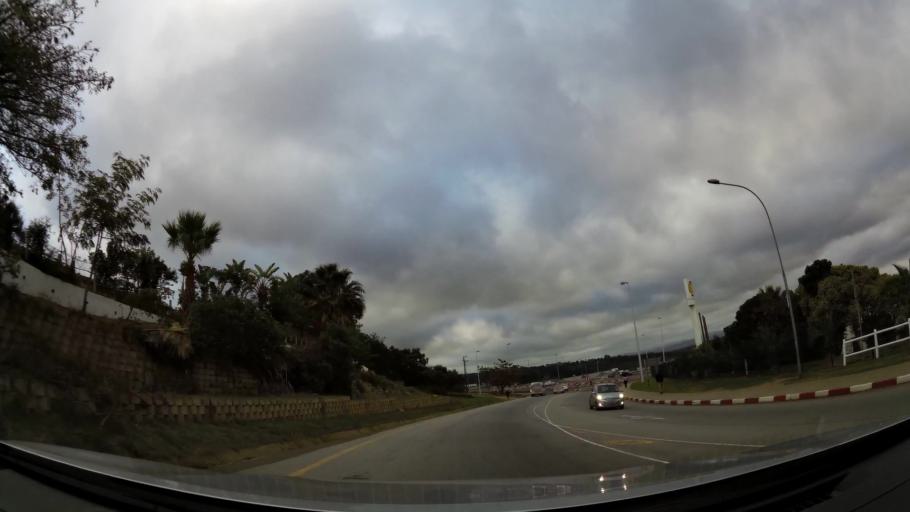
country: ZA
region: Western Cape
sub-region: Eden District Municipality
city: Plettenberg Bay
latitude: -34.0508
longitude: 23.3579
